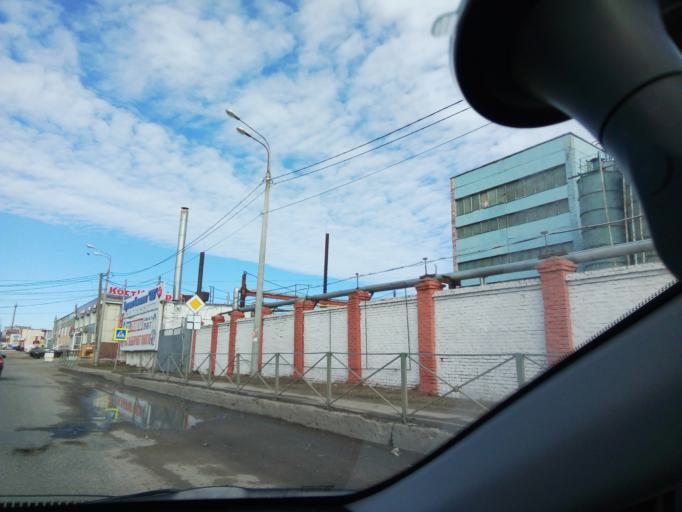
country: RU
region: Chuvashia
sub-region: Cheboksarskiy Rayon
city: Cheboksary
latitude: 56.1045
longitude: 47.2518
